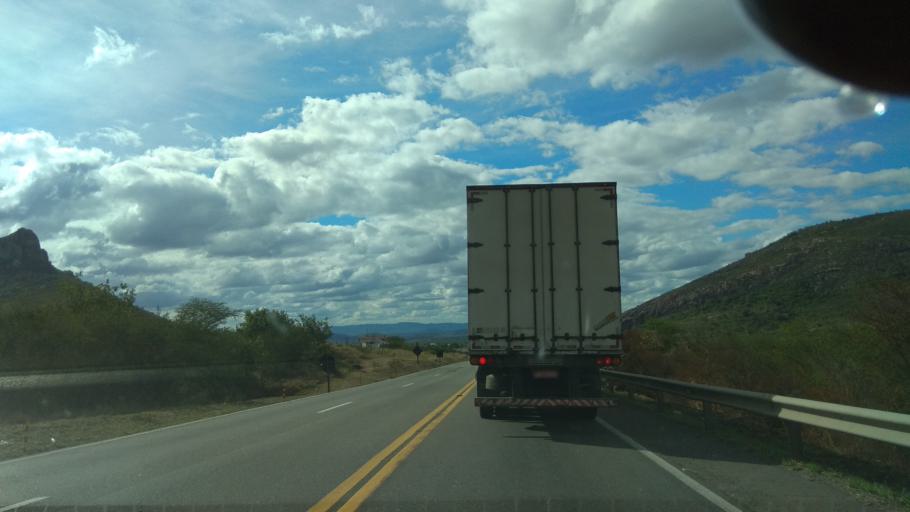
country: BR
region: Bahia
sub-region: Amargosa
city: Amargosa
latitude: -12.8836
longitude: -39.8588
